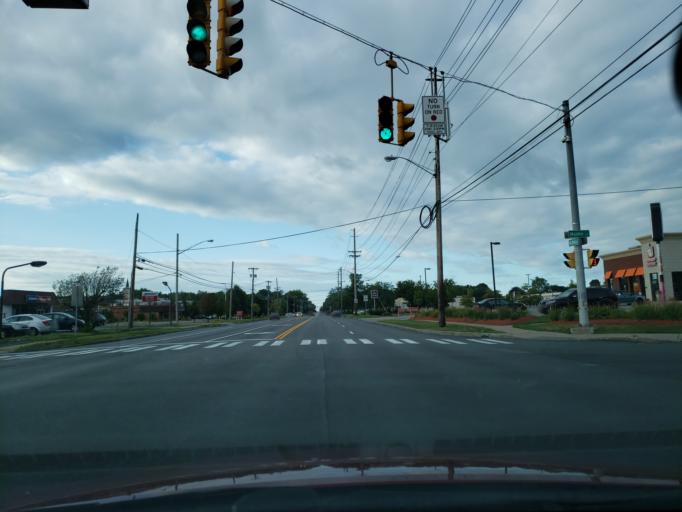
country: US
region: New York
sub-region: Monroe County
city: Greece
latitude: 43.2237
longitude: -77.6590
